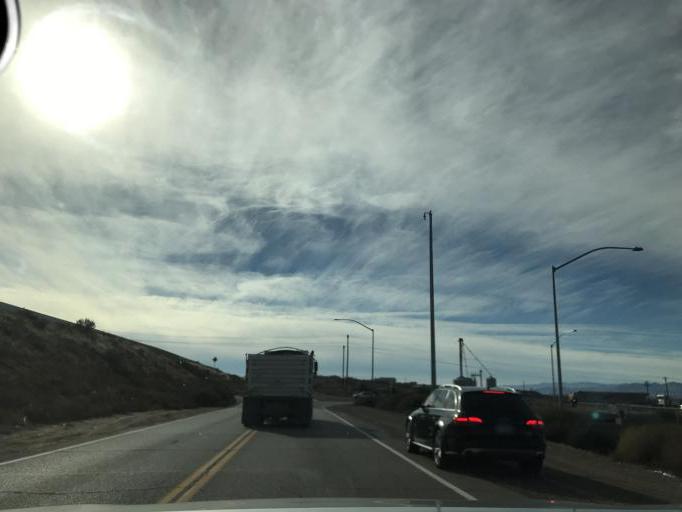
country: US
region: Nevada
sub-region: Clark County
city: Moapa Town
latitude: 36.6616
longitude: -114.5738
